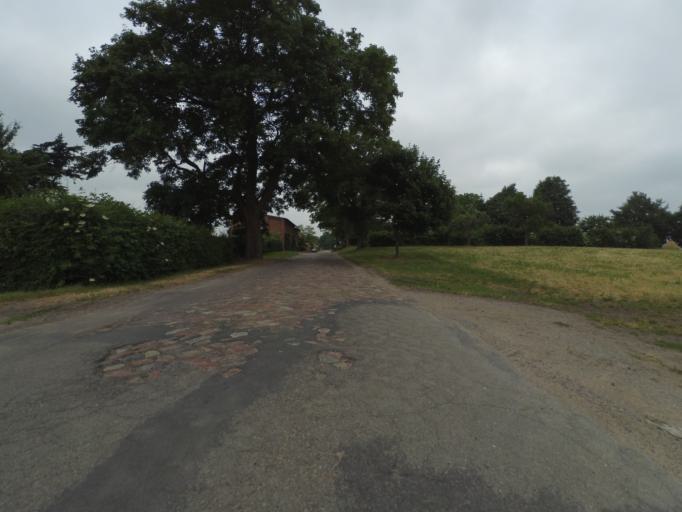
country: DE
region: Mecklenburg-Vorpommern
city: Lubz
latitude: 53.5158
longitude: 12.0363
